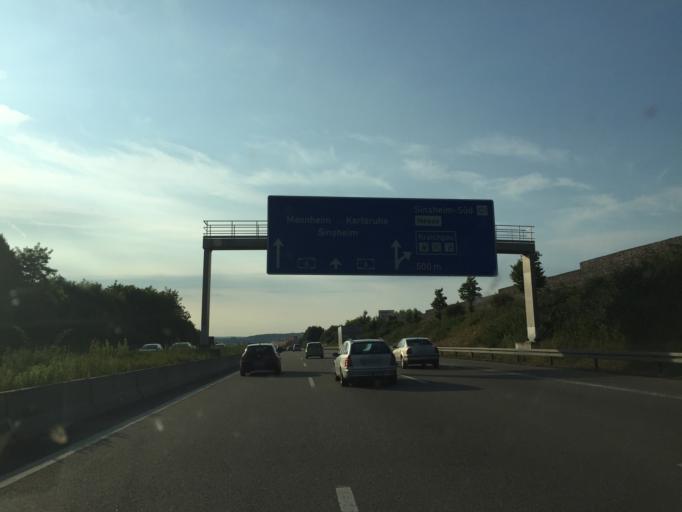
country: DE
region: Baden-Wuerttemberg
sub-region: Karlsruhe Region
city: Sinsheim
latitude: 49.2346
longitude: 8.9011
